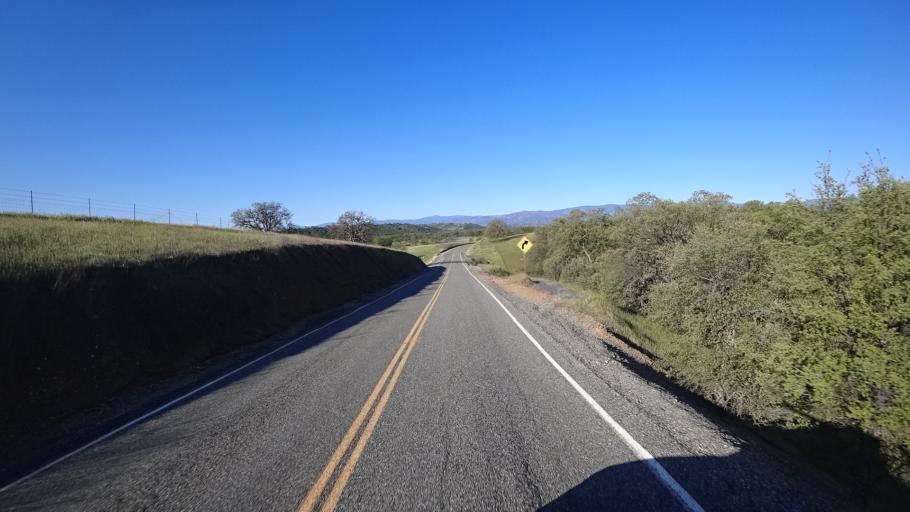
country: US
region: California
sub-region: Tehama County
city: Rancho Tehama Reserve
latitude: 39.8115
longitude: -122.4044
